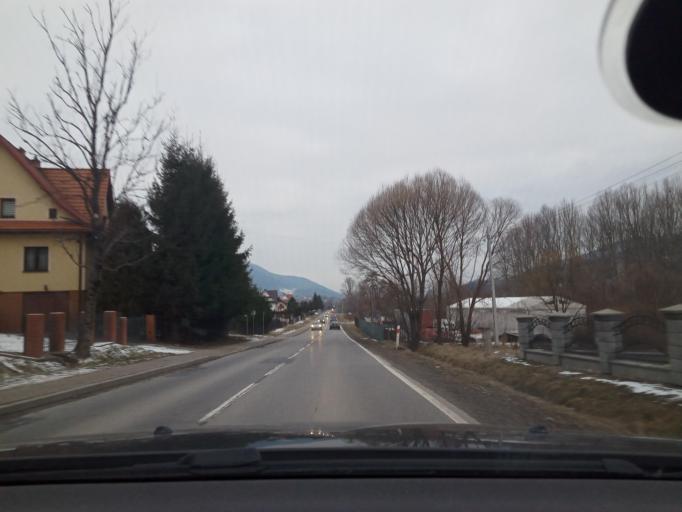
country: PL
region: Lesser Poland Voivodeship
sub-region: Powiat limanowski
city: Mszana Gorna
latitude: 49.6598
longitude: 20.1008
